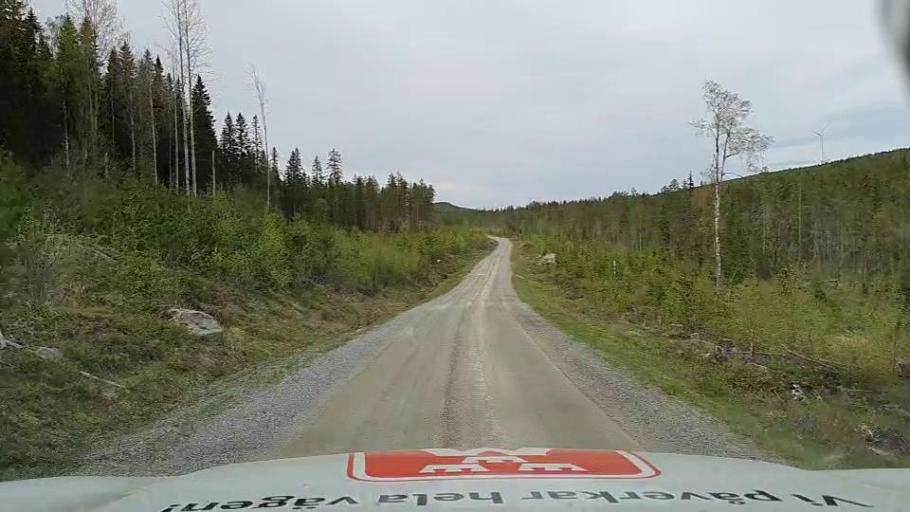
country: SE
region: Jaemtland
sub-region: Bergs Kommun
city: Hoverberg
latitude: 62.5474
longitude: 14.8979
